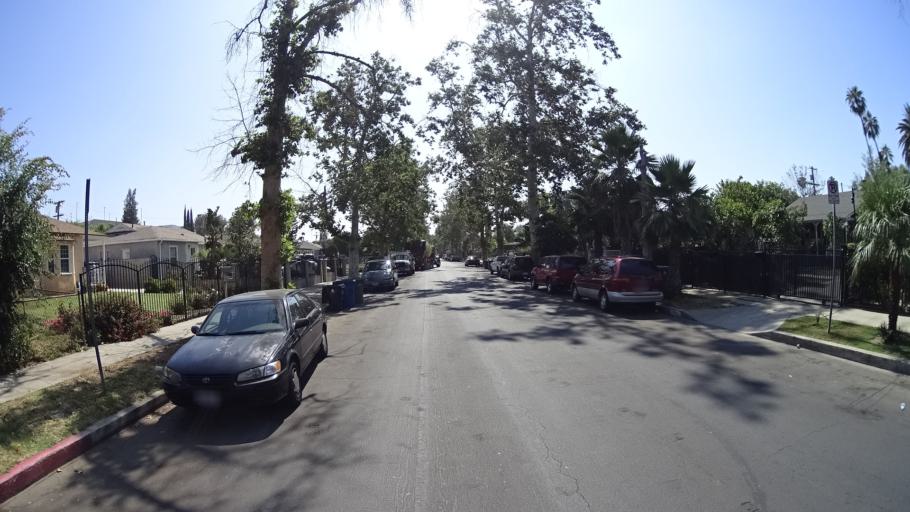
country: US
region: California
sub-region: Los Angeles County
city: Van Nuys
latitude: 34.1984
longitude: -118.4529
